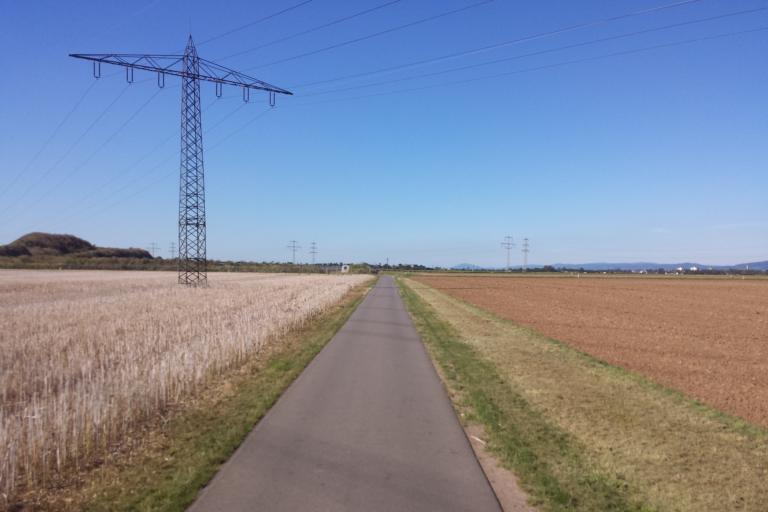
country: DE
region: Baden-Wuerttemberg
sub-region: Karlsruhe Region
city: Plankstadt
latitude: 49.4206
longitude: 8.5872
